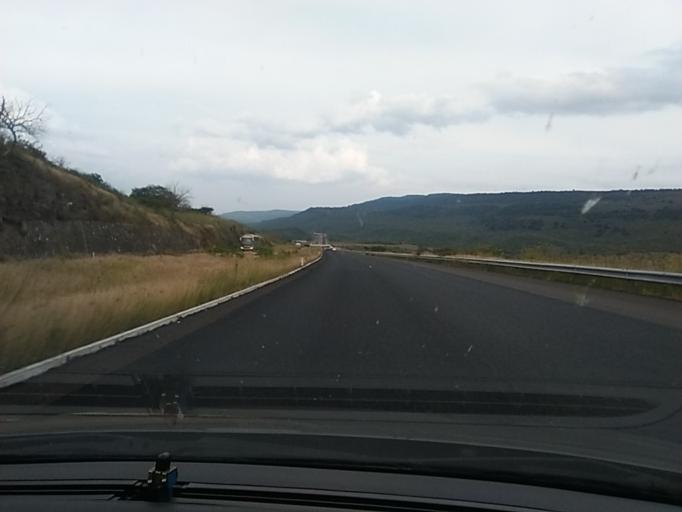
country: MX
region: Mexico
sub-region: Chapultepec
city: Chucandiro
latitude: 19.8731
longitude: -101.3912
